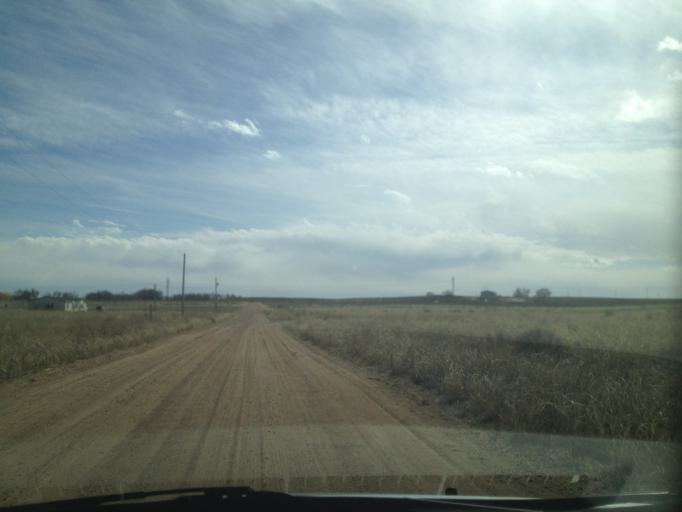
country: US
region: Colorado
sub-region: Weld County
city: Keenesburg
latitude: 40.2879
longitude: -104.2554
